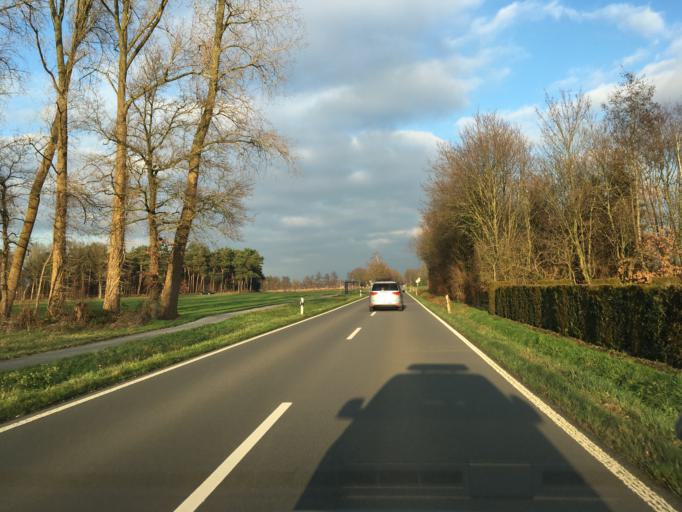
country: DE
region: North Rhine-Westphalia
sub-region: Regierungsbezirk Munster
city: Gronau
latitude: 52.1515
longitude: 7.0183
